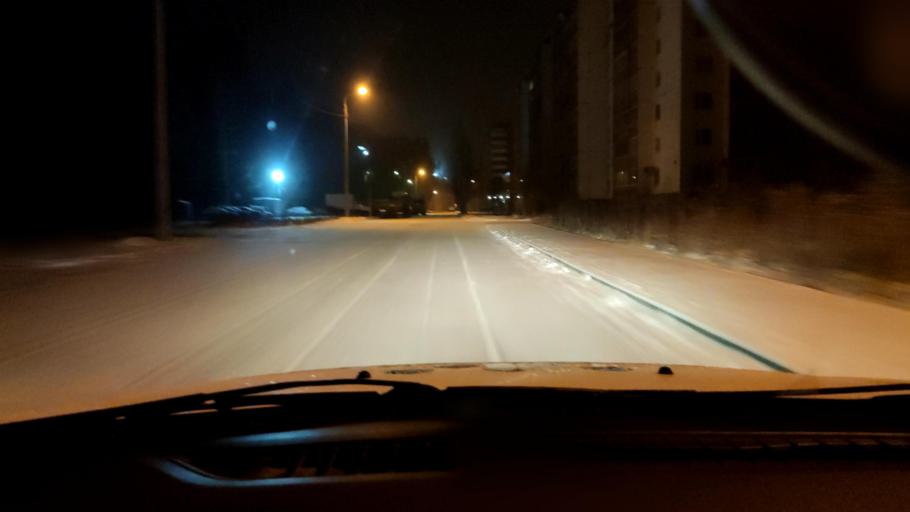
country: RU
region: Perm
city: Kondratovo
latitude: 58.0210
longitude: 56.0056
